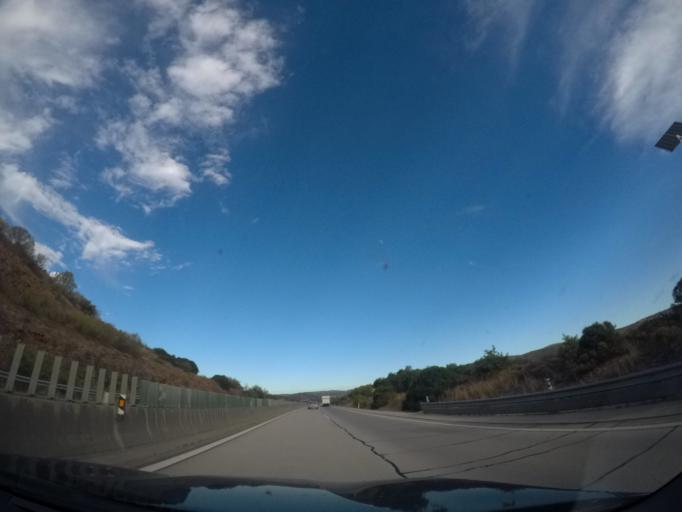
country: PT
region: Faro
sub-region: Loule
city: Vilamoura
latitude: 37.1250
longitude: -8.0860
